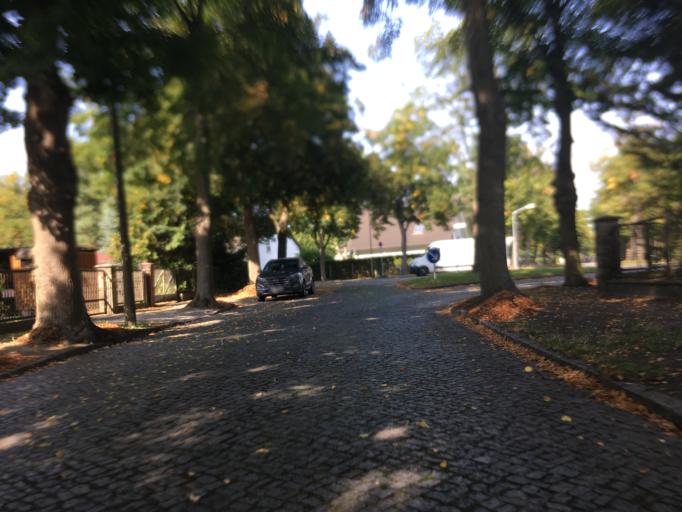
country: DE
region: Brandenburg
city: Zeuthen
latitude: 52.3682
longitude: 13.6296
